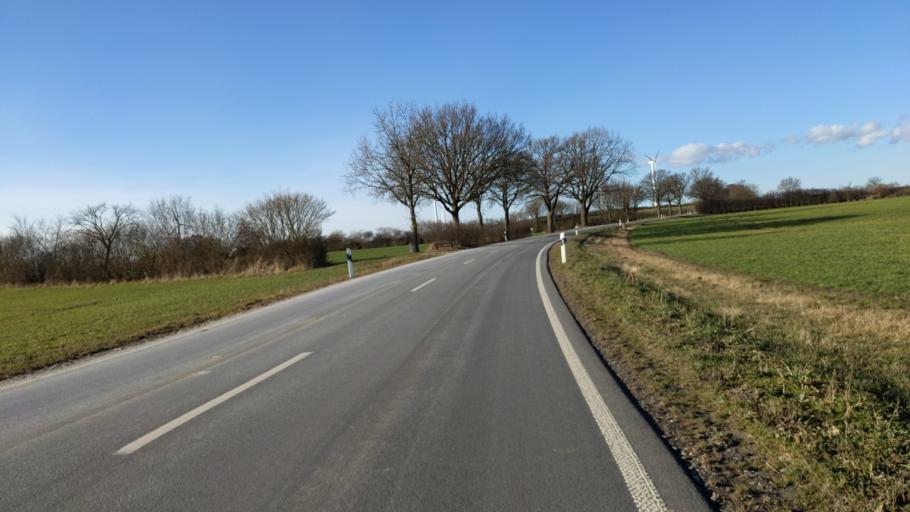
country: DE
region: Schleswig-Holstein
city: Susel
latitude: 54.0501
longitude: 10.6551
